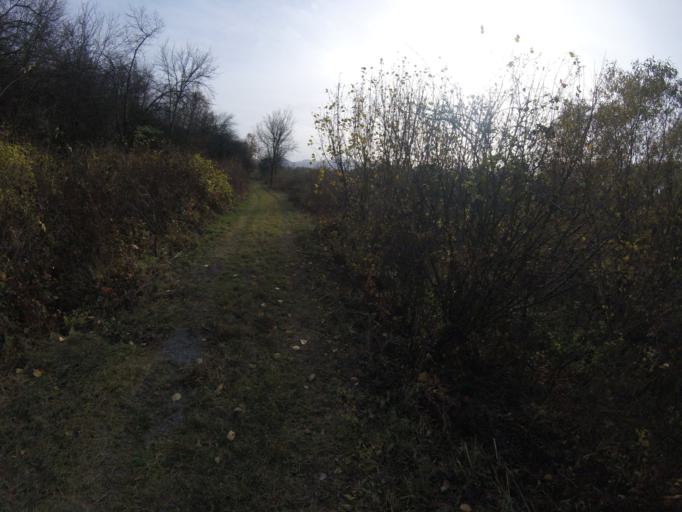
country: HU
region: Borsod-Abauj-Zemplen
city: Gonc
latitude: 48.5038
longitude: 21.4512
